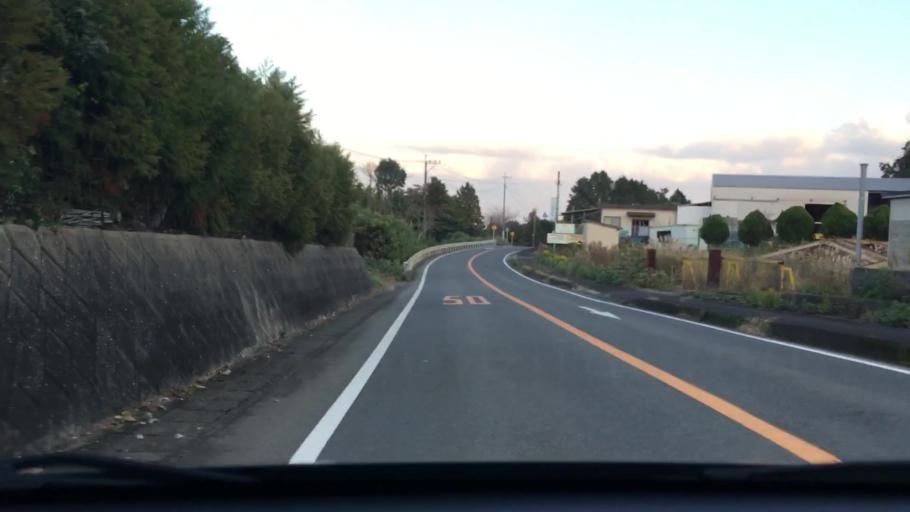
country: JP
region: Nagasaki
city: Sasebo
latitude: 33.0440
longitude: 129.7054
